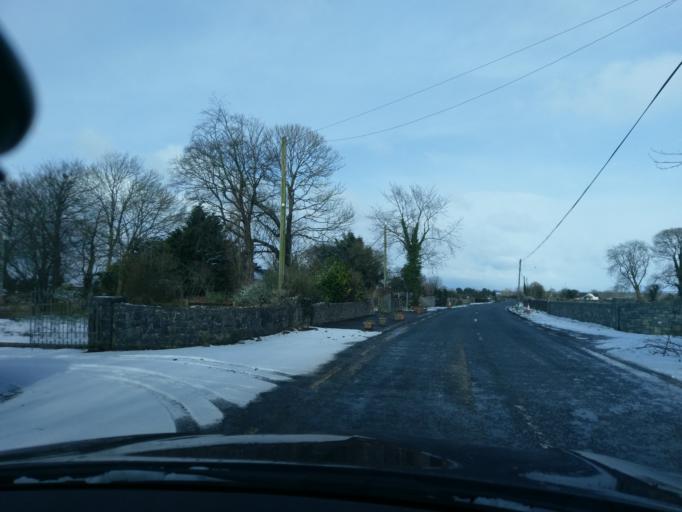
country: IE
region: Connaught
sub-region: County Galway
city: Athenry
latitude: 53.1873
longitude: -8.7674
